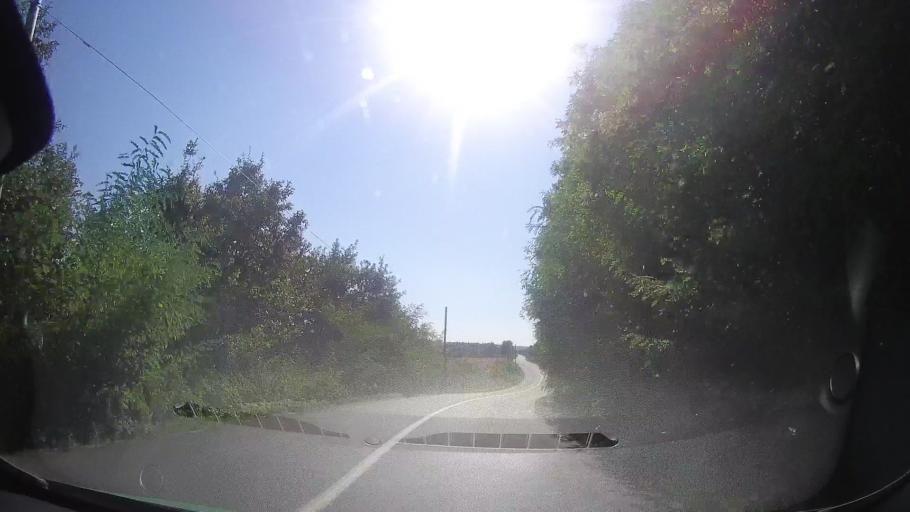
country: RO
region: Timis
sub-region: Comuna Ohaba Lunga
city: Ohaba Lunga
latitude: 45.8817
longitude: 21.9642
